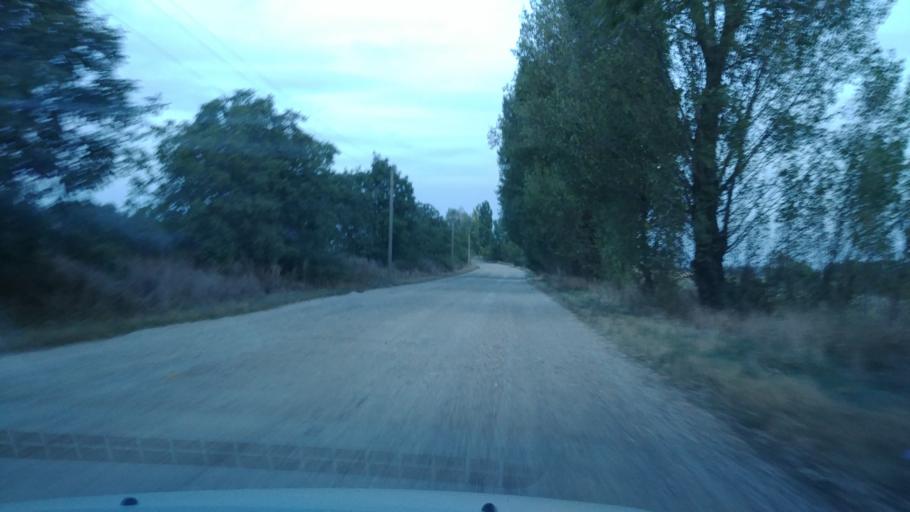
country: MD
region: Rezina
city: Saharna
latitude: 47.6774
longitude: 28.9251
